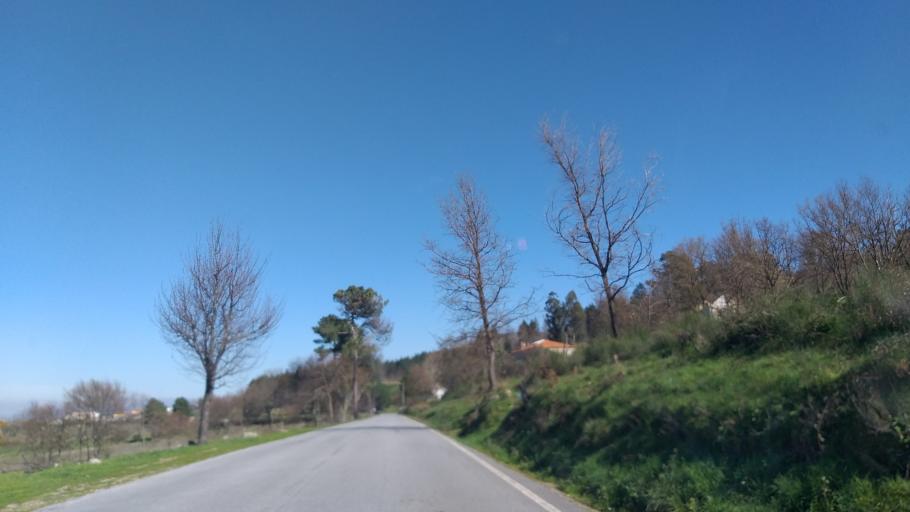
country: PT
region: Guarda
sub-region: Manteigas
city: Manteigas
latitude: 40.4821
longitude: -7.6126
